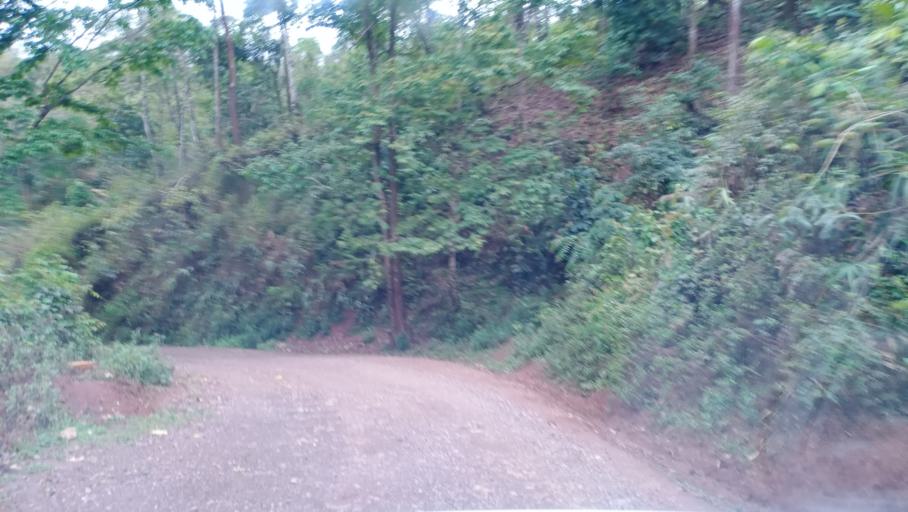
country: LA
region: Phongsali
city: Phongsali
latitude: 21.3400
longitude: 102.0760
